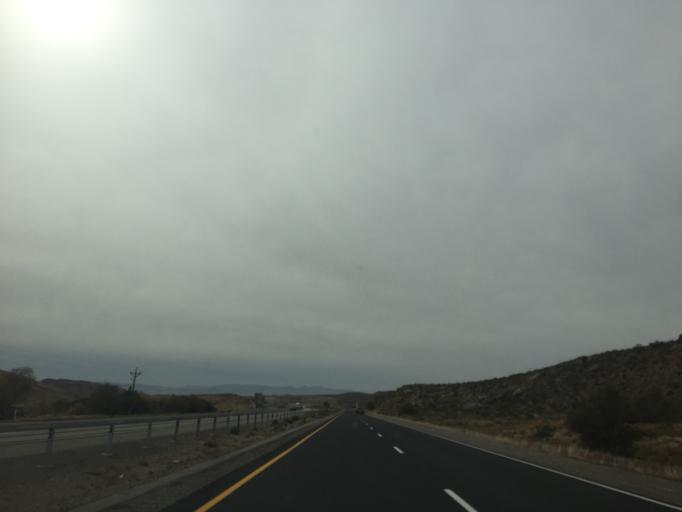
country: US
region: Utah
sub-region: Washington County
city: Toquerville
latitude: 37.2245
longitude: -113.3800
